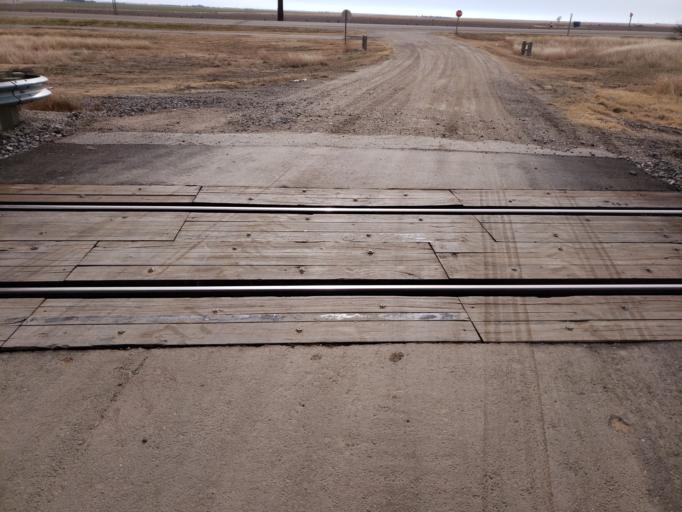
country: US
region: Kansas
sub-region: Clark County
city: Ashland
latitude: 37.5239
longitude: -99.7599
